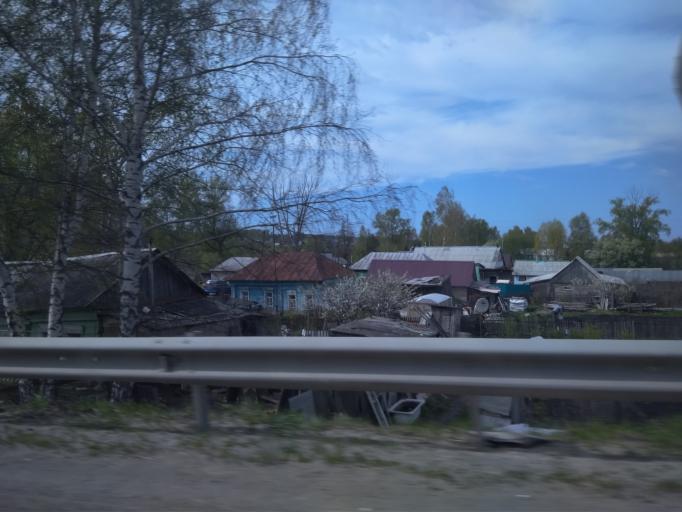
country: RU
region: Mordoviya
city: Atemar
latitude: 54.3202
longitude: 45.4832
